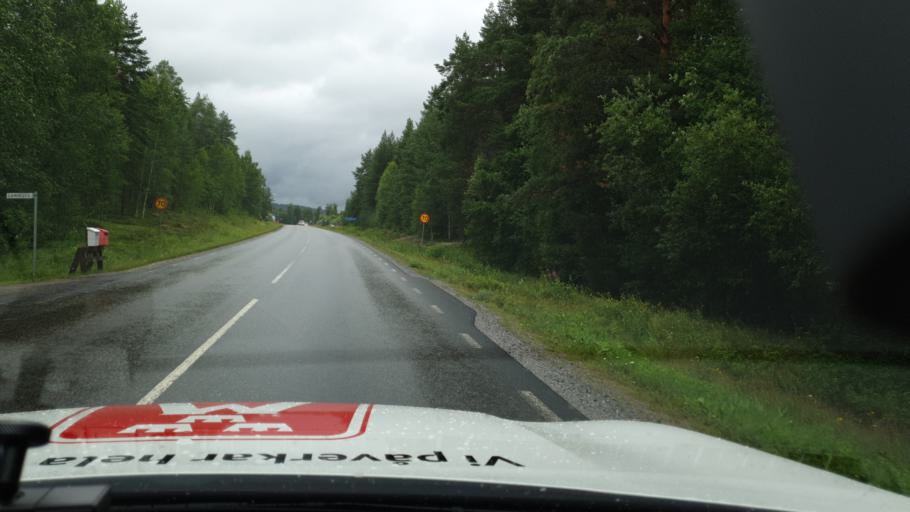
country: SE
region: Norrbotten
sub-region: Pitea Kommun
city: Roknas
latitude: 65.3420
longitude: 21.1435
